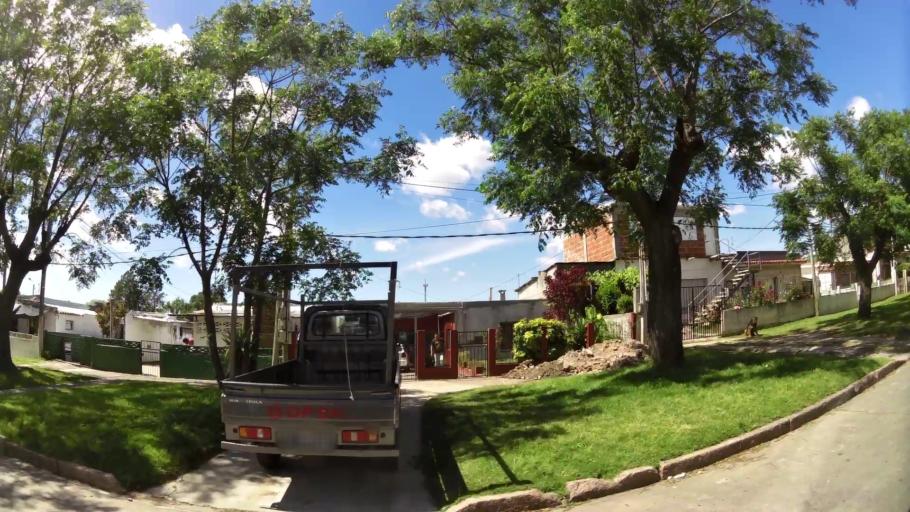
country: UY
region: Montevideo
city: Montevideo
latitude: -34.8390
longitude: -56.1338
